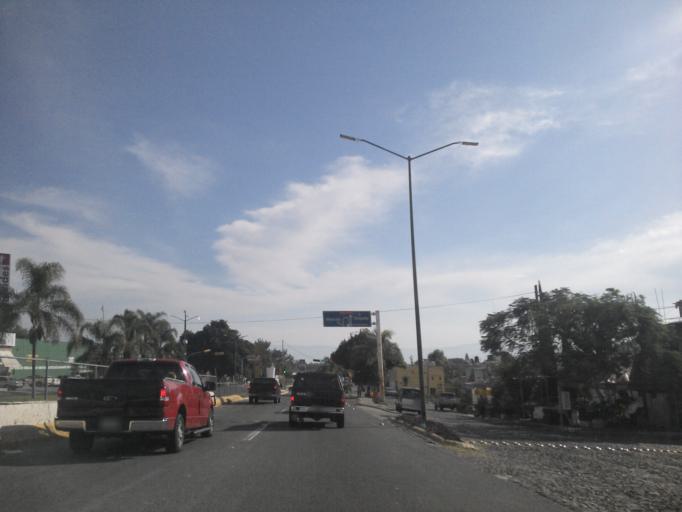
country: MX
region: Jalisco
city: Chapala
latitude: 20.3016
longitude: -103.1910
